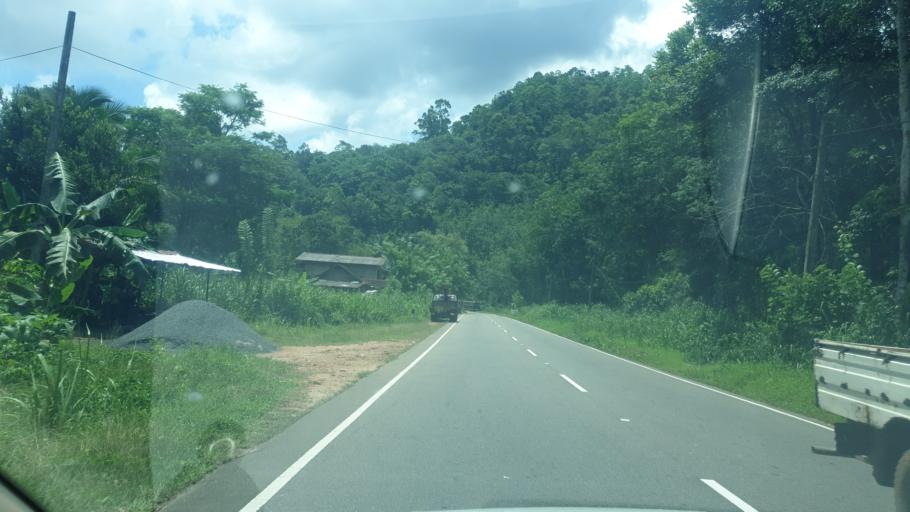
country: LK
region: Western
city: Horawala Junction
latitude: 6.5387
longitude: 80.2715
